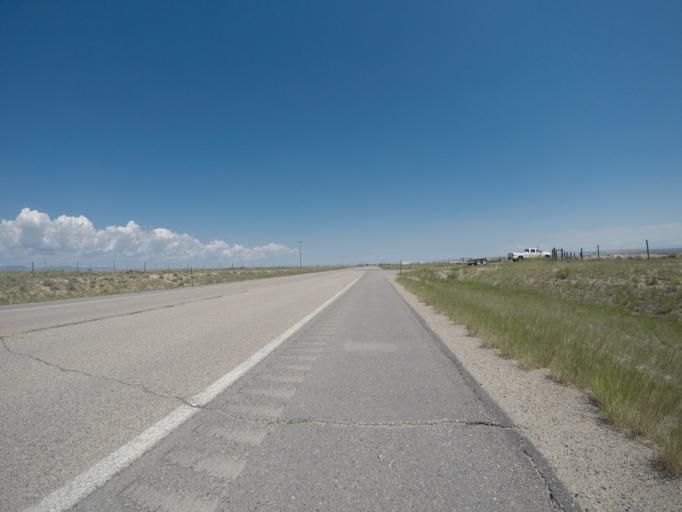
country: US
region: Wyoming
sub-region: Sublette County
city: Marbleton
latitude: 42.5017
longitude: -110.1050
